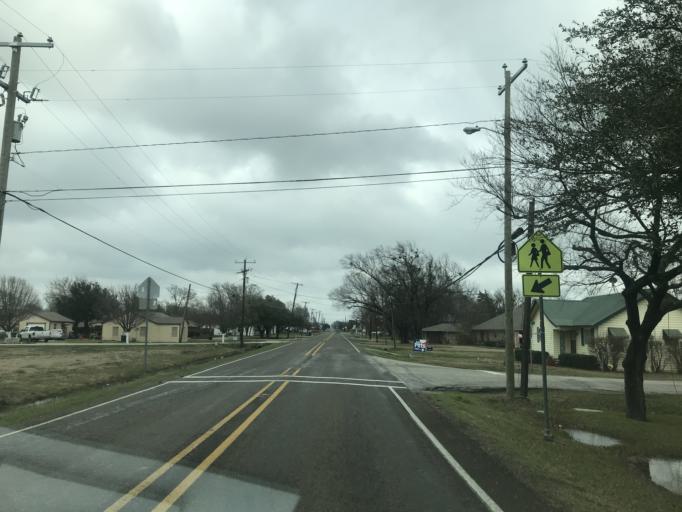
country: US
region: Texas
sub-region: Ellis County
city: Palmer
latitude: 32.4298
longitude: -96.6740
